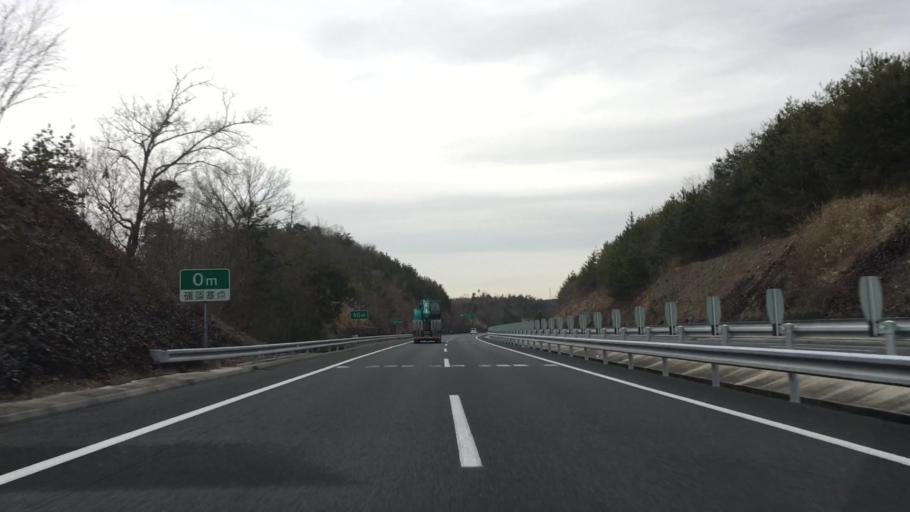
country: JP
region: Gifu
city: Toki
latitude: 35.3104
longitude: 137.1782
